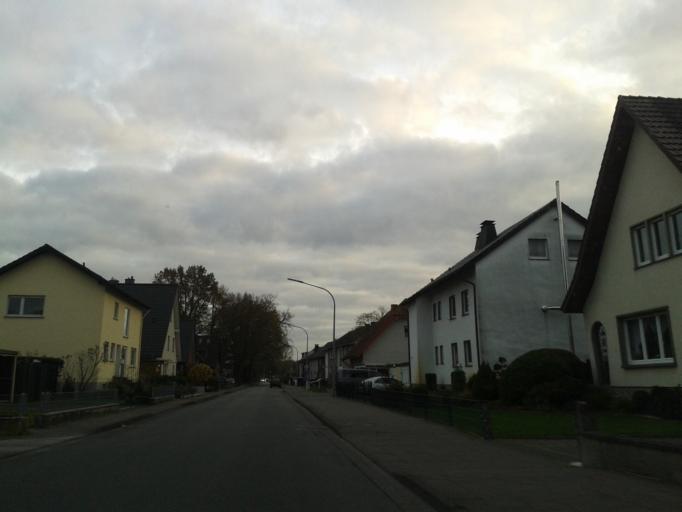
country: DE
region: North Rhine-Westphalia
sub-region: Regierungsbezirk Detmold
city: Paderborn
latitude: 51.7592
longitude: 8.7309
